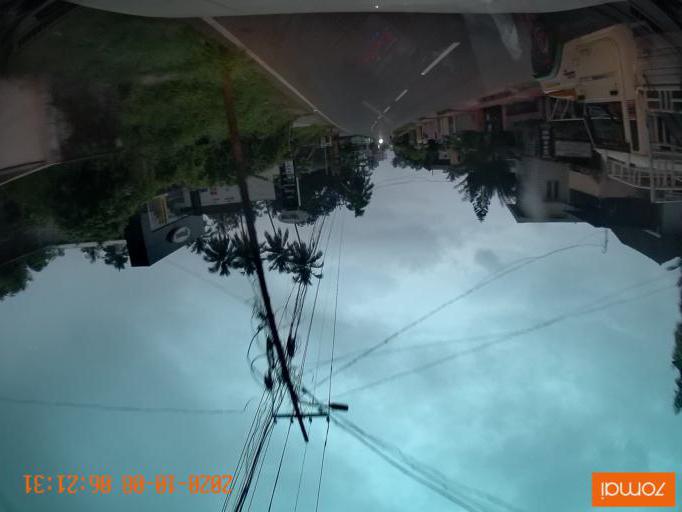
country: IN
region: Kerala
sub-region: Thrissur District
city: Trichur
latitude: 10.5211
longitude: 76.2310
